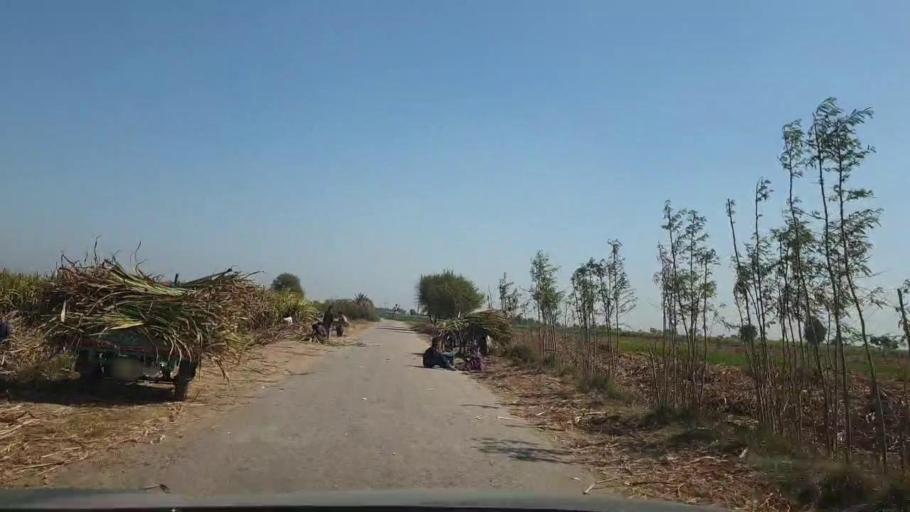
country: PK
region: Sindh
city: Tando Adam
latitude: 25.6301
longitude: 68.6732
